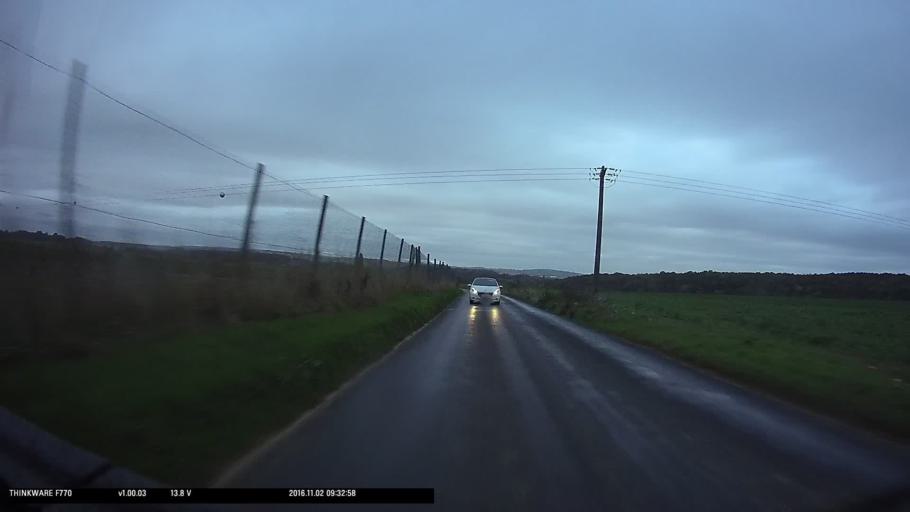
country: FR
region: Ile-de-France
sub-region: Departement du Val-d'Oise
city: Courdimanche
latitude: 49.0658
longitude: 2.0037
